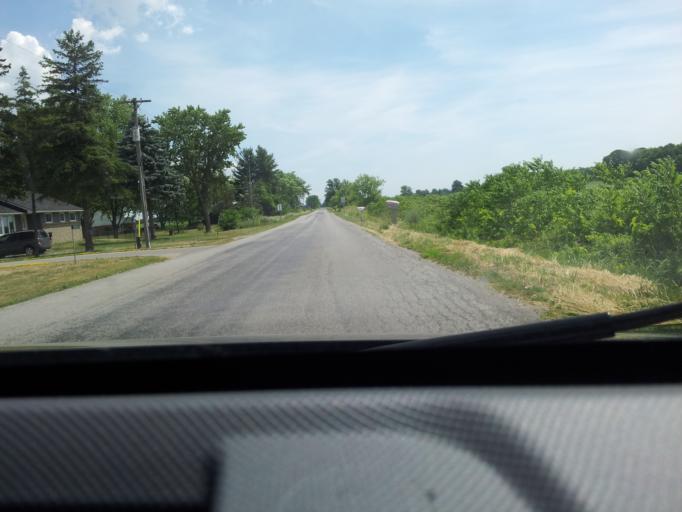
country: CA
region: Ontario
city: Norfolk County
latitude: 42.8253
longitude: -80.2759
